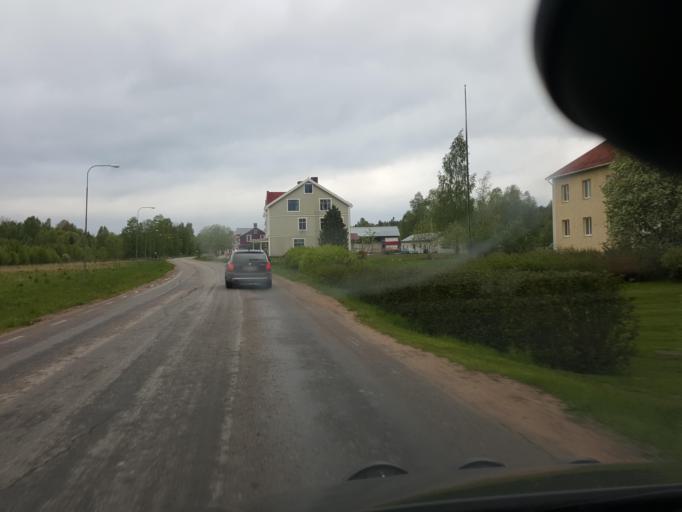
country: SE
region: Gaevleborg
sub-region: Ljusdals Kommun
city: Jaervsoe
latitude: 61.7944
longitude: 16.2048
